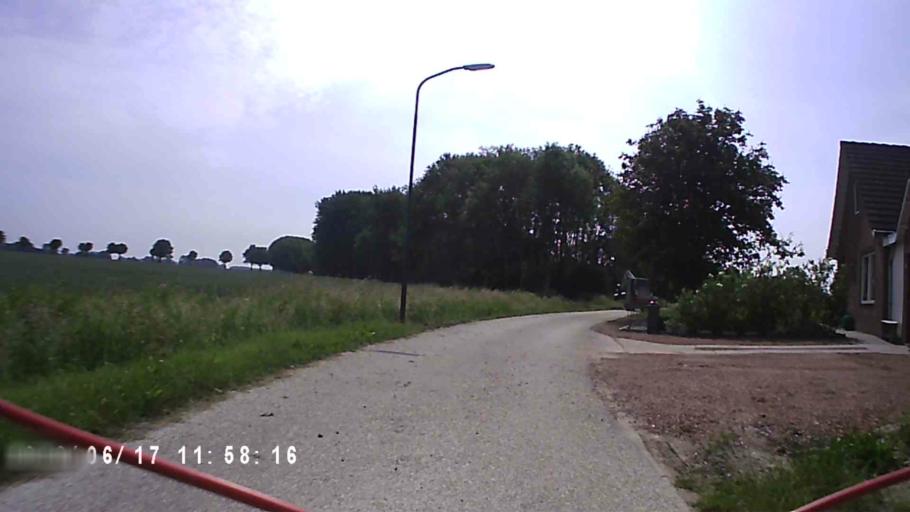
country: NL
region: Groningen
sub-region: Gemeente De Marne
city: Ulrum
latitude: 53.3444
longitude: 6.3274
